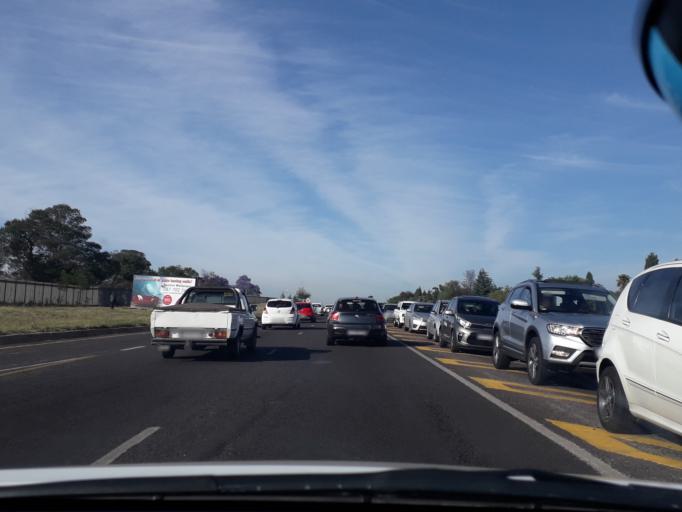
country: ZA
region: Gauteng
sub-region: City of Johannesburg Metropolitan Municipality
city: Roodepoort
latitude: -26.1053
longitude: 27.9244
